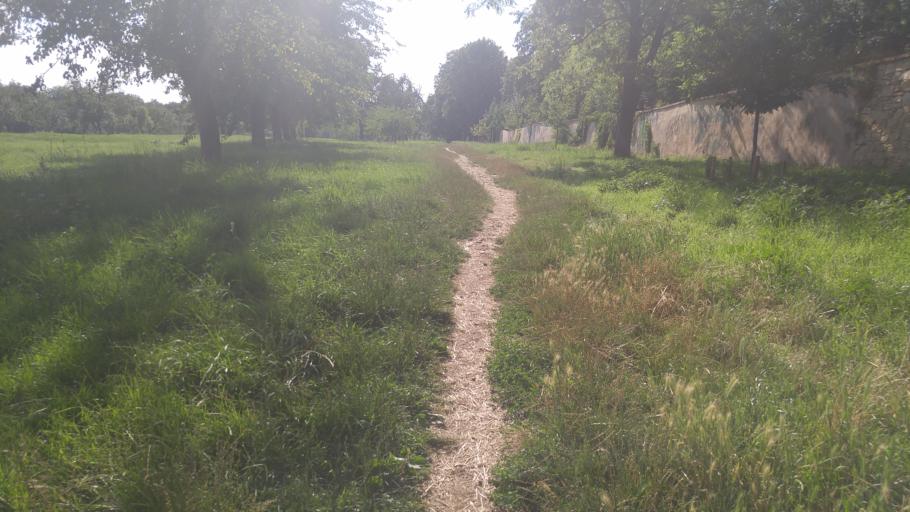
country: CZ
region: Praha
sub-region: Praha 1
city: Mala Strana
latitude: 50.0873
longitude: 14.3598
